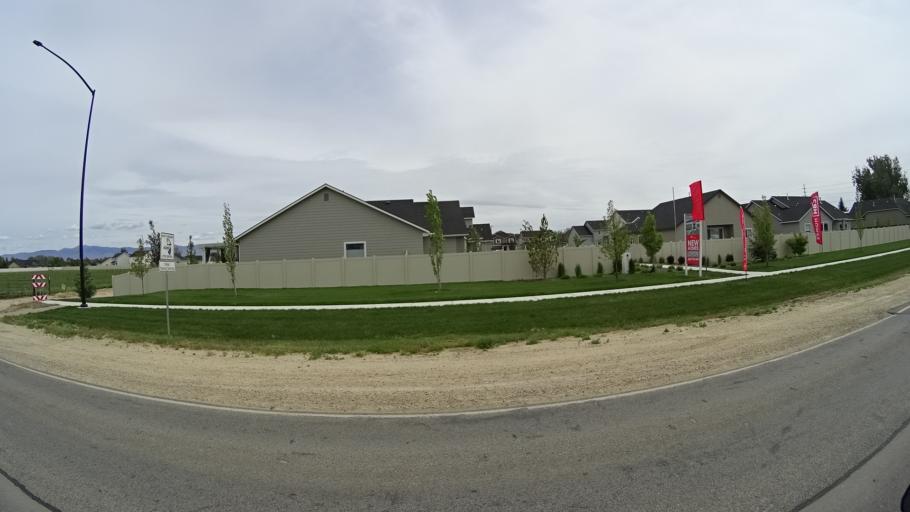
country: US
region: Idaho
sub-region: Ada County
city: Meridian
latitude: 43.5629
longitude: -116.3545
